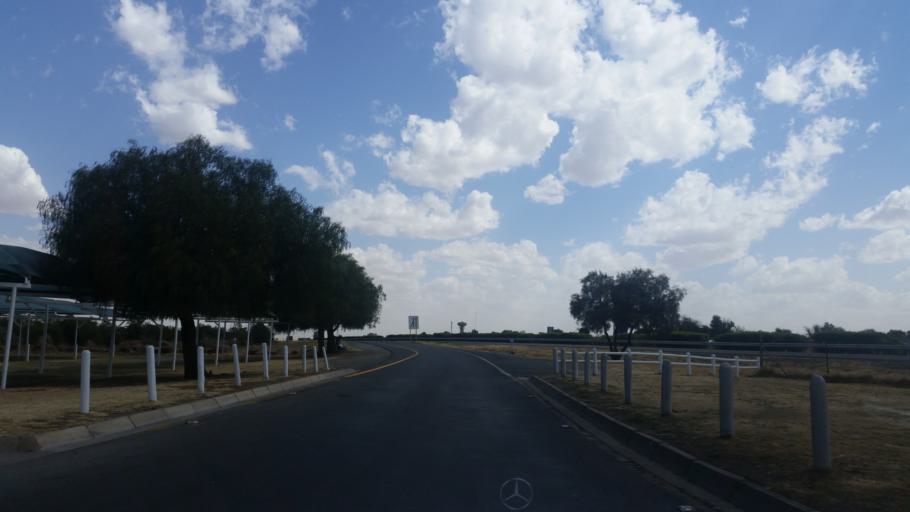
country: ZA
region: Orange Free State
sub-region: Mangaung Metropolitan Municipality
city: Bloemfontein
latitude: -29.0754
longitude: 26.1822
